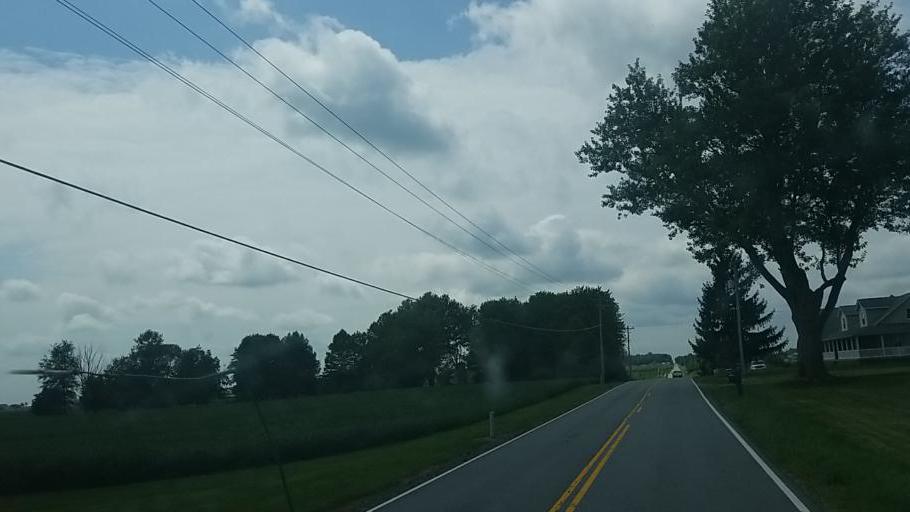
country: US
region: Ohio
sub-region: Fairfield County
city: Lithopolis
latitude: 39.7487
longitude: -82.7828
